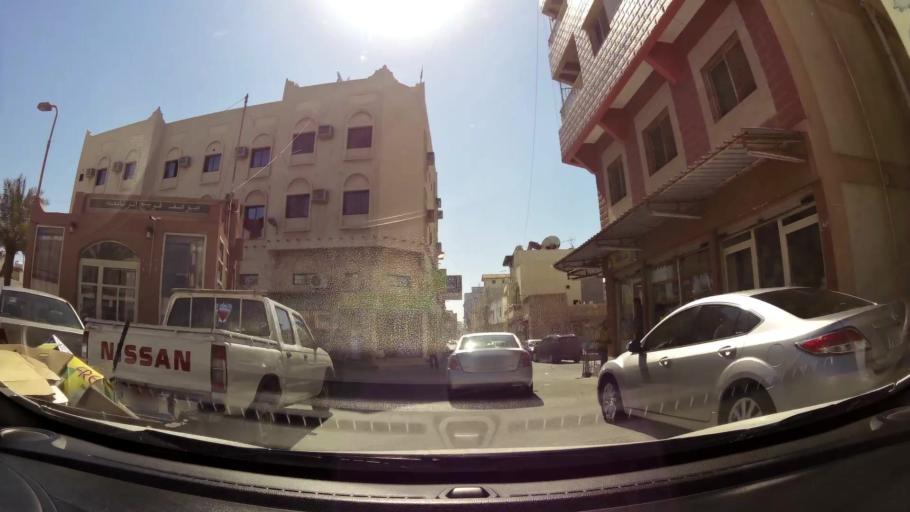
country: BH
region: Muharraq
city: Al Muharraq
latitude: 26.2483
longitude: 50.6115
